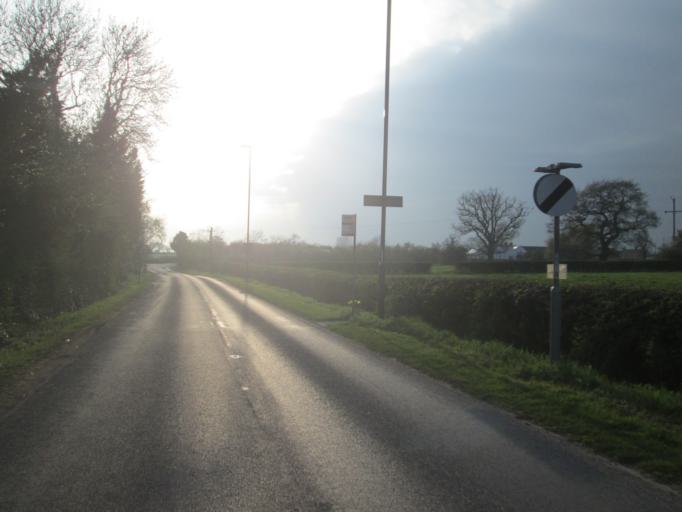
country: GB
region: England
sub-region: Derbyshire
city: Findern
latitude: 52.9243
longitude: -1.5419
